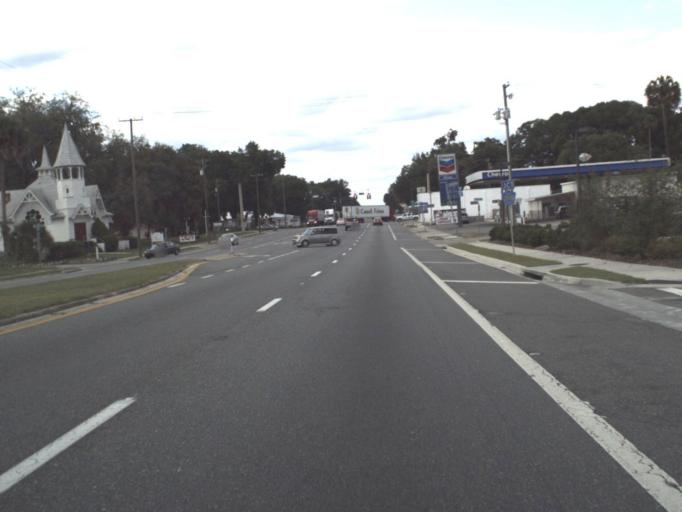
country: US
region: Florida
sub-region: Marion County
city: Citra
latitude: 29.4146
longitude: -82.1099
